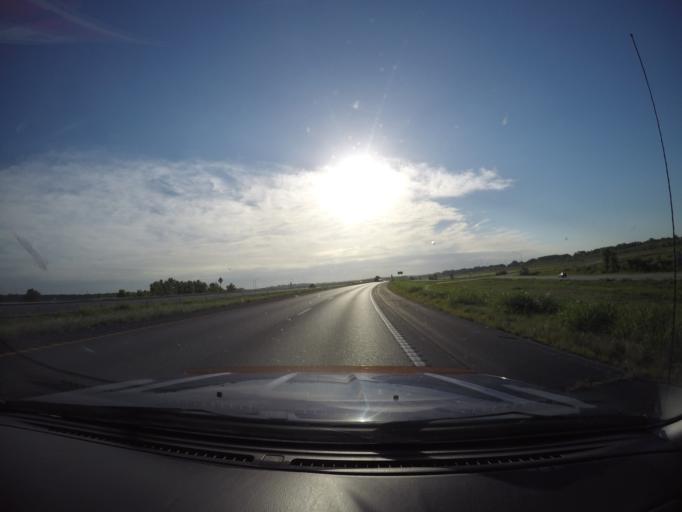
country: US
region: Missouri
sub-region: Platte County
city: Riverside
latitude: 39.1601
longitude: -94.6441
